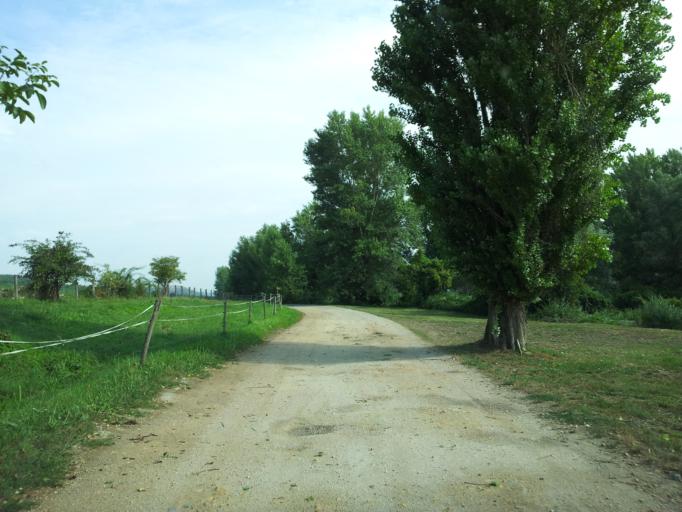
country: HU
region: Veszprem
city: Badacsonytomaj
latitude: 46.8372
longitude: 17.5512
